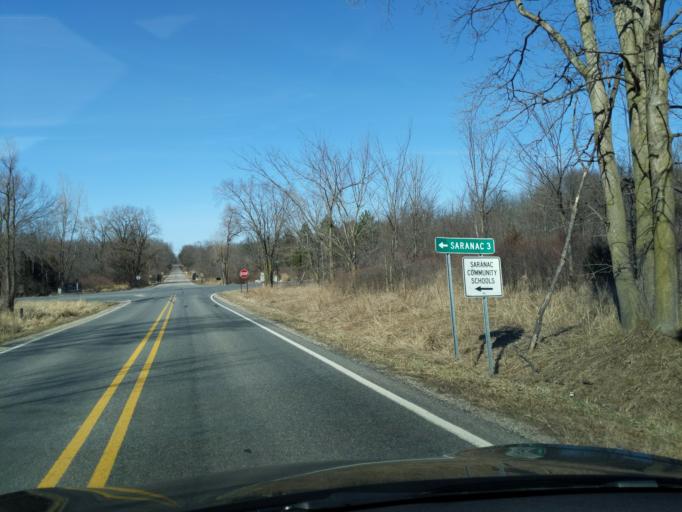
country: US
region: Michigan
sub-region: Ionia County
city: Saranac
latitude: 42.9290
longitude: -85.1341
